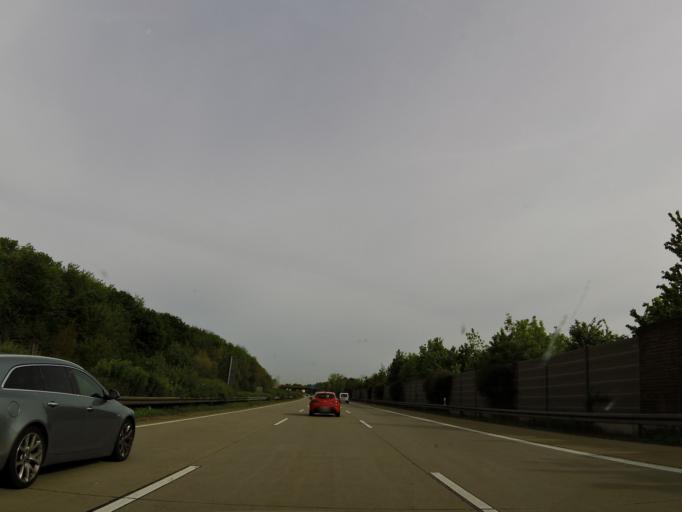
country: DE
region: Lower Saxony
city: Hildesheim
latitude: 52.1709
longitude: 9.9827
